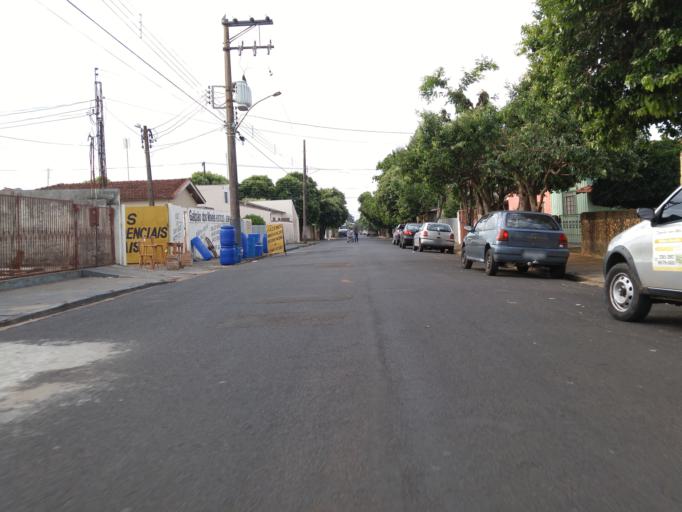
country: BR
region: Sao Paulo
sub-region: Paraguacu Paulista
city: Paraguacu Paulista
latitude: -22.4248
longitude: -50.5790
